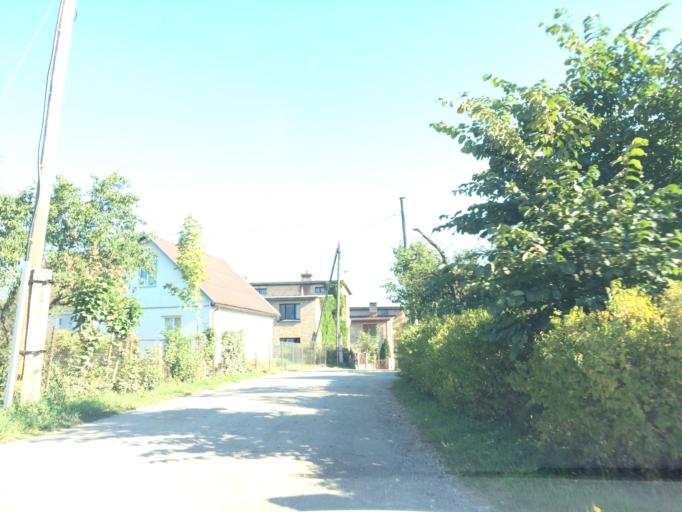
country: LV
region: Rezekne
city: Rezekne
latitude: 56.5020
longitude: 27.3428
